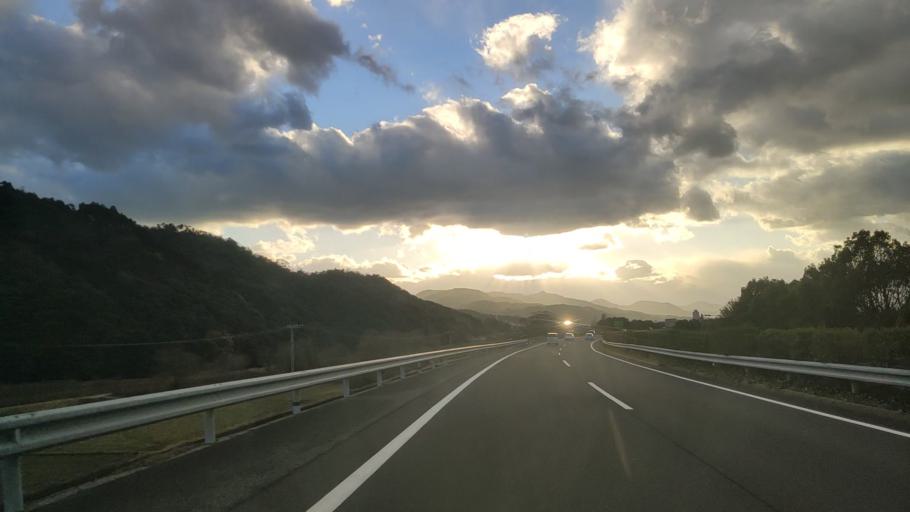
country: JP
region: Ehime
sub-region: Shikoku-chuo Shi
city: Matsuyama
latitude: 33.7899
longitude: 132.8950
